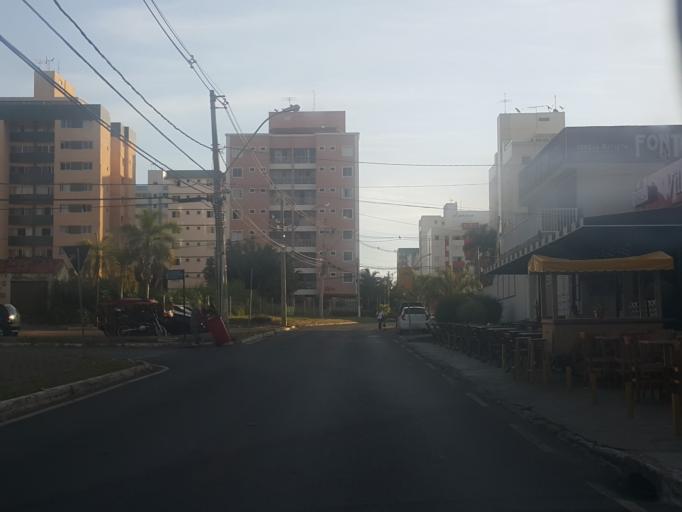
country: BR
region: Federal District
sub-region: Brasilia
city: Brasilia
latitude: -15.8291
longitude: -48.0139
